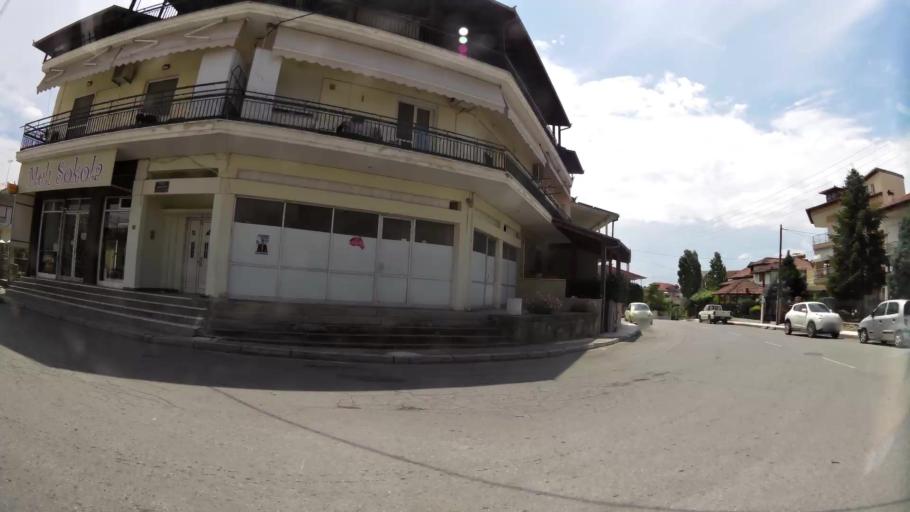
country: GR
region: Central Macedonia
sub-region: Nomos Pierias
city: Katerini
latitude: 40.2631
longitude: 22.4999
